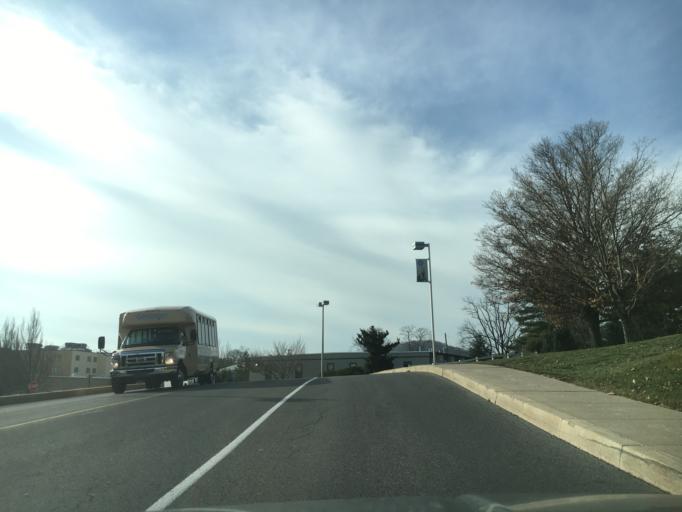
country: US
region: Pennsylvania
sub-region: Montour County
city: Danville
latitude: 40.9698
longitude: -76.6041
